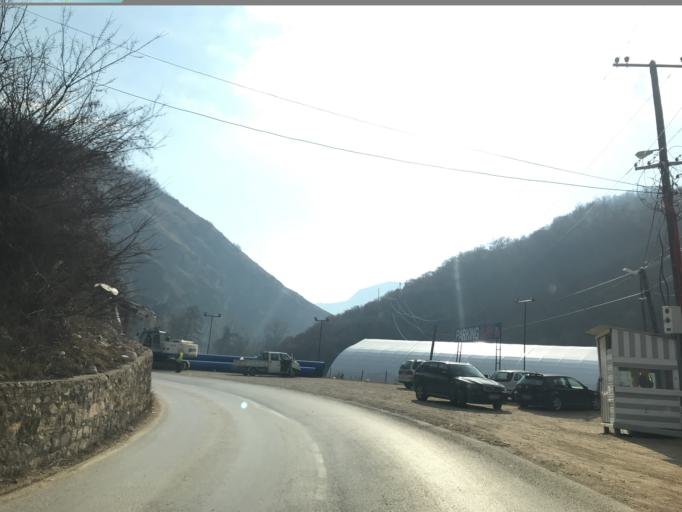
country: XK
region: Prizren
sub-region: Prizren
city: Prizren
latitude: 42.2101
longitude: 20.7483
